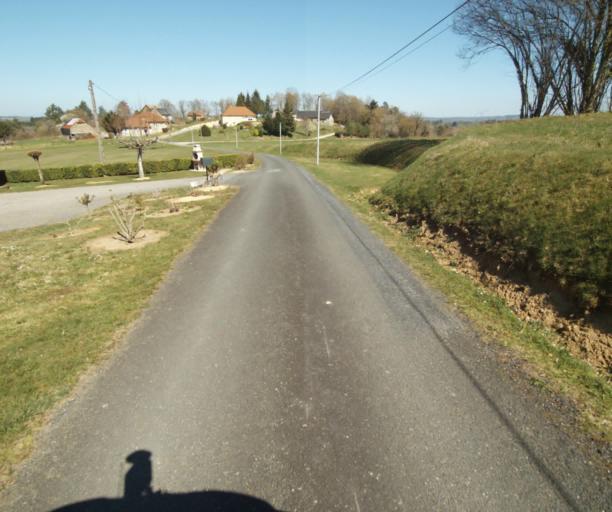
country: FR
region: Limousin
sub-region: Departement de la Correze
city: Chameyrat
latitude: 45.2717
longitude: 1.7105
